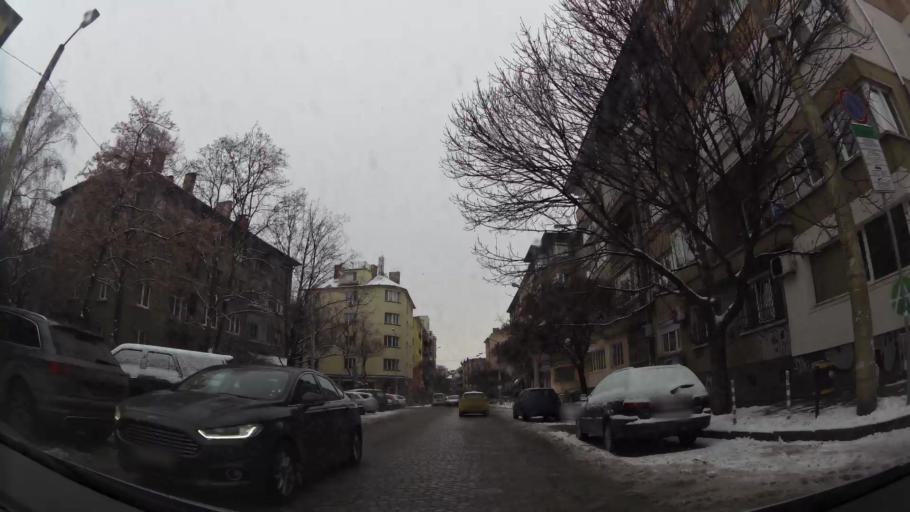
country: BG
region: Sofia-Capital
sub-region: Stolichna Obshtina
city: Sofia
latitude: 42.6883
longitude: 23.3457
